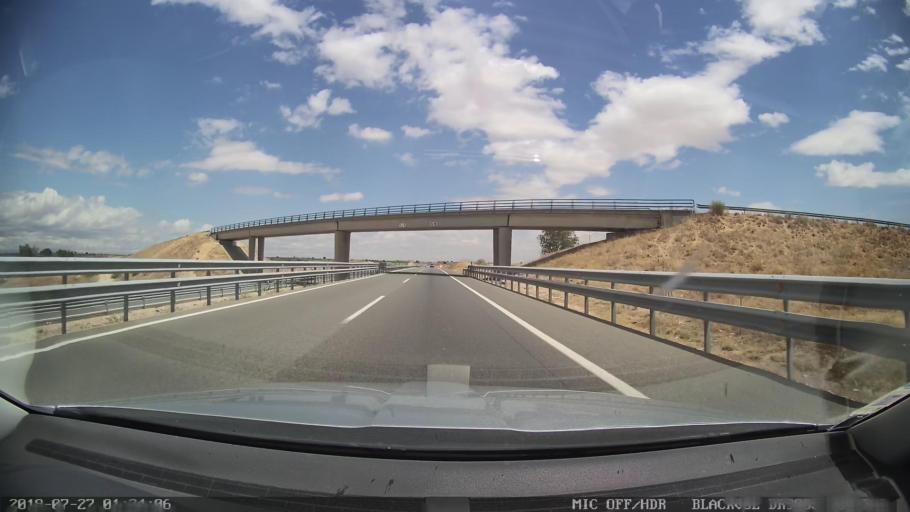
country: ES
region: Castille-La Mancha
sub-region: Province of Toledo
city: Santa Cruz del Retamar
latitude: 40.1275
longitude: -4.2164
